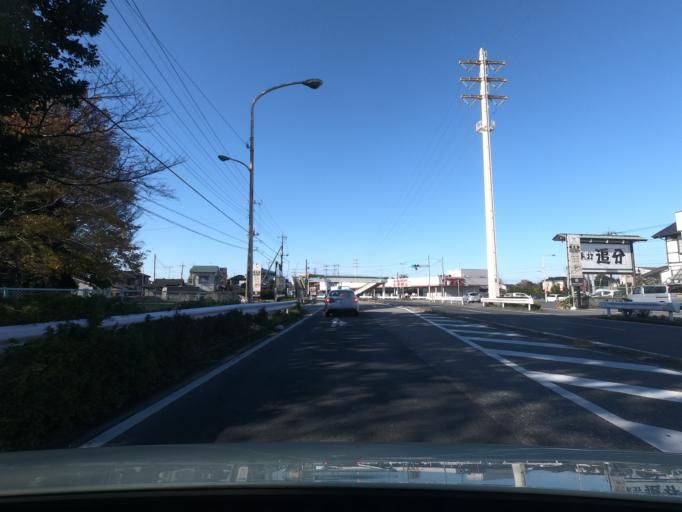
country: JP
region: Ibaraki
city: Ishige
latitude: 36.1834
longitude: 139.9496
